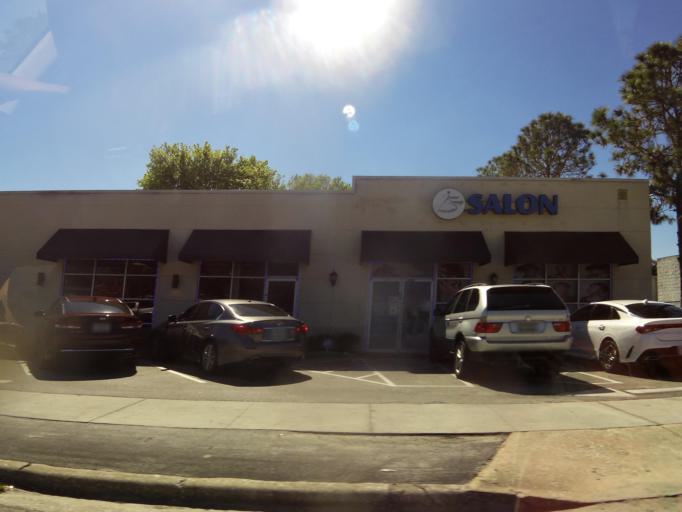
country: US
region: Florida
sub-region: Orange County
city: Lockhart
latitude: 28.6185
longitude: -81.4409
